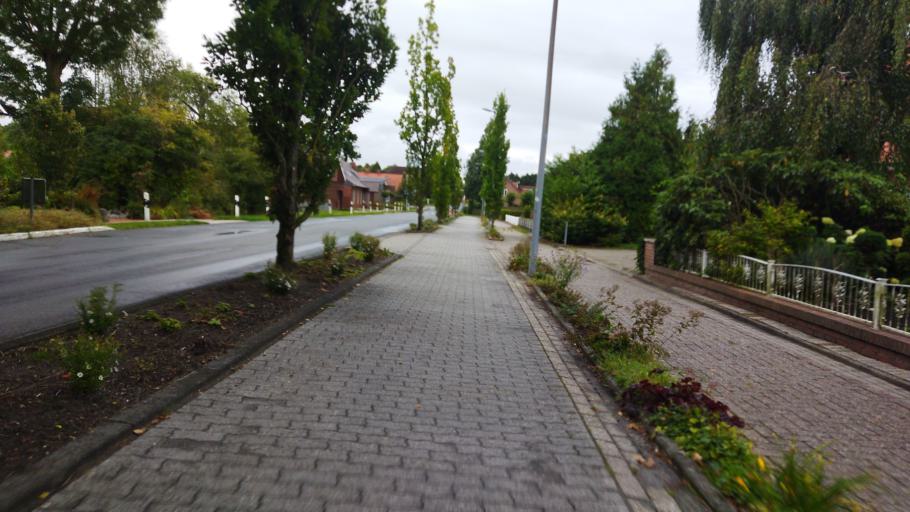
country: DE
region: Lower Saxony
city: Hinte
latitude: 53.4174
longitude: 7.1921
